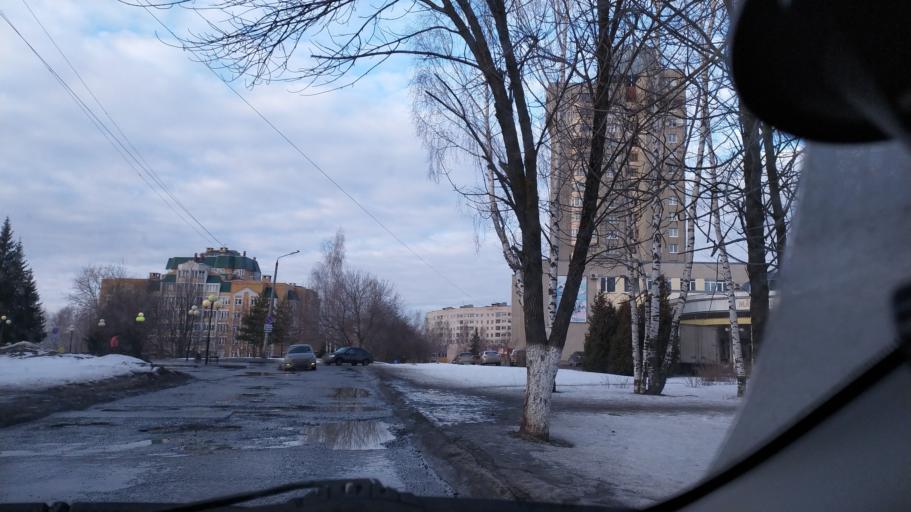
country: RU
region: Chuvashia
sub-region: Cheboksarskiy Rayon
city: Cheboksary
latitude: 56.1456
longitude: 47.2162
